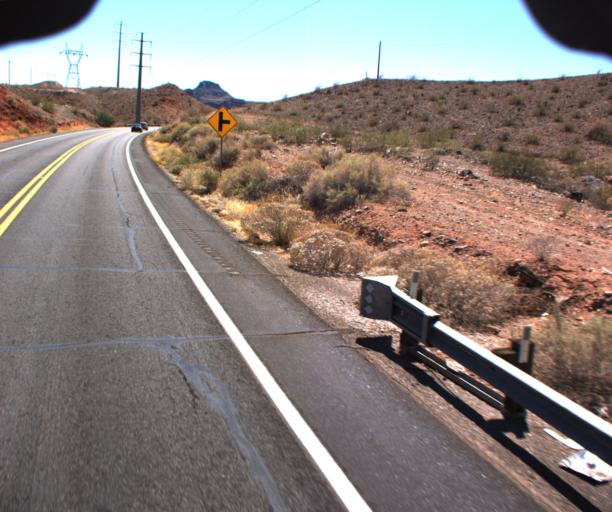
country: US
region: Arizona
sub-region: La Paz County
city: Cienega Springs
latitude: 34.2799
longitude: -114.1310
